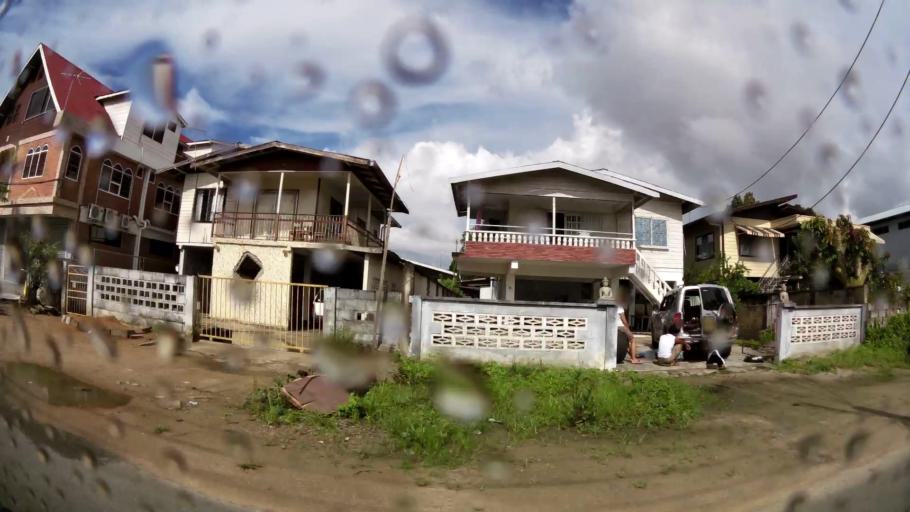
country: SR
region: Paramaribo
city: Paramaribo
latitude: 5.8432
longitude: -55.2065
